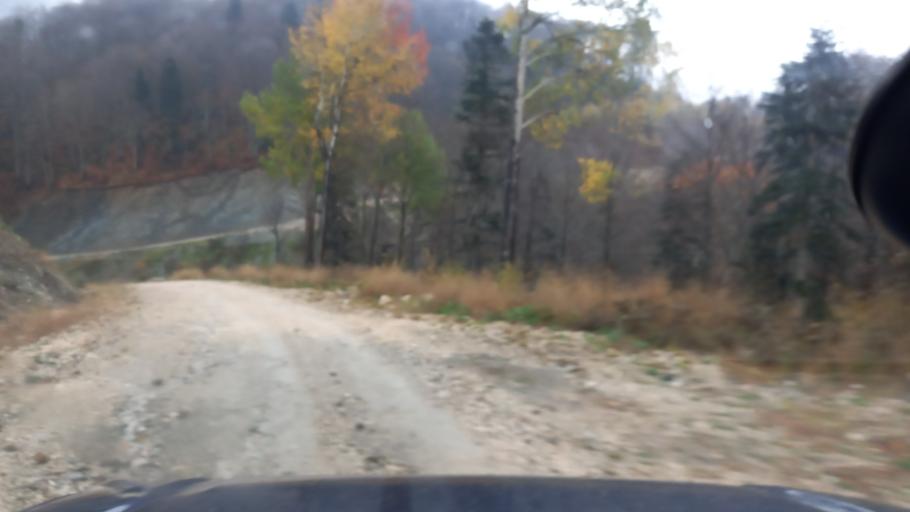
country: RU
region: Krasnodarskiy
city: Dagomys
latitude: 43.9874
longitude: 39.8482
